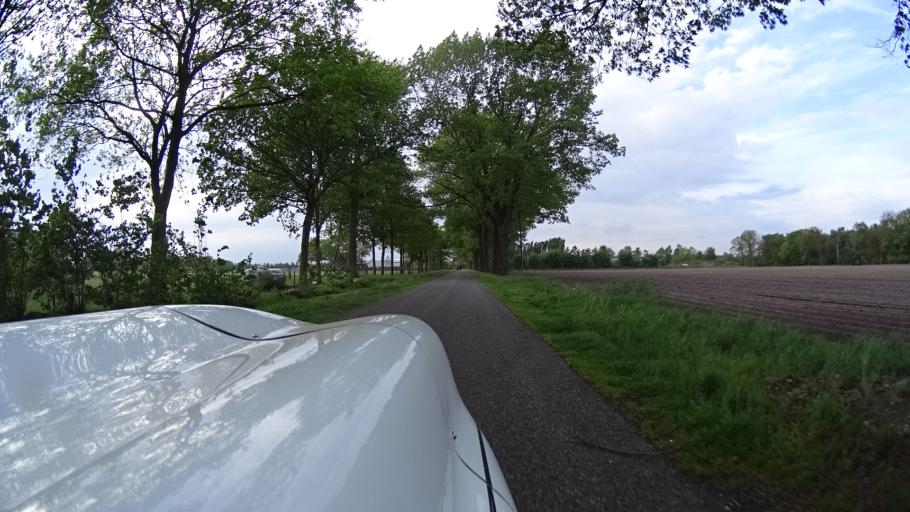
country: NL
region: North Brabant
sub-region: Gemeente Mill en Sint Hubert
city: Wilbertoord
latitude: 51.5892
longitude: 5.7922
